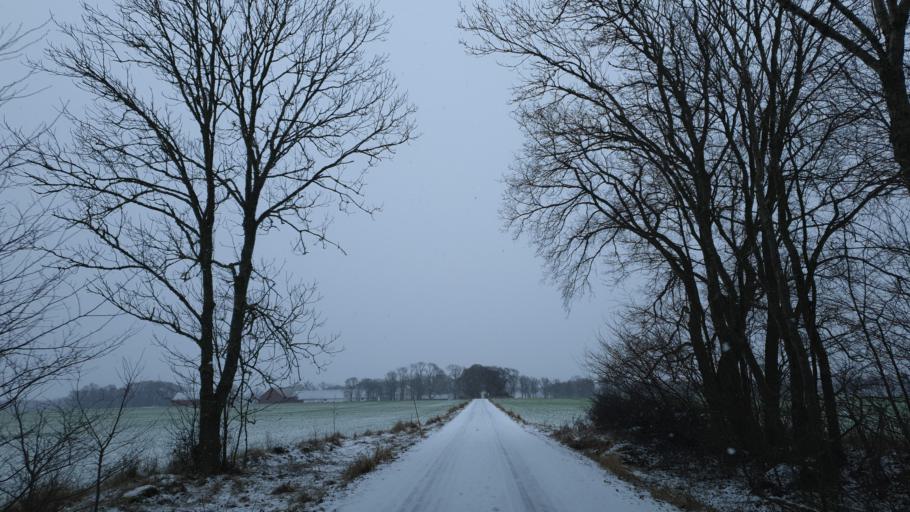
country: SE
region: Gotland
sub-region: Gotland
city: Visby
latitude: 57.5198
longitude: 18.4539
